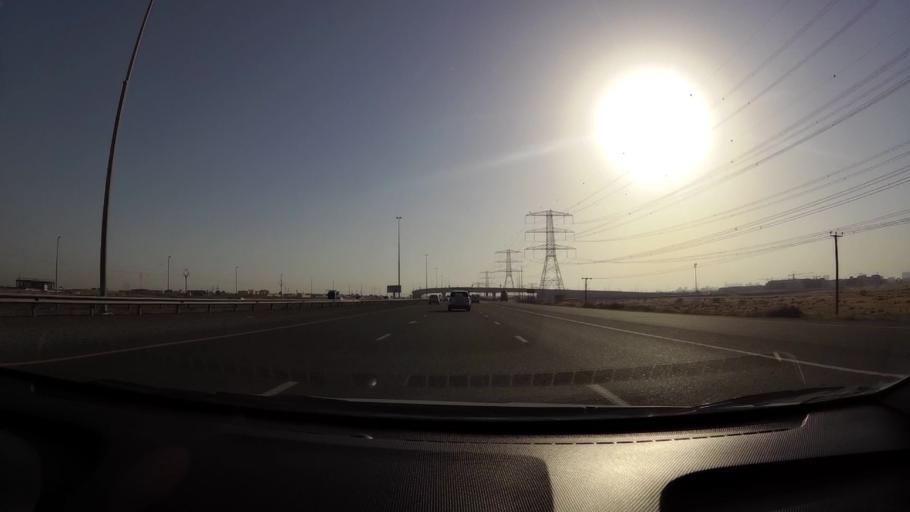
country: AE
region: Ajman
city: Ajman
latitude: 25.3601
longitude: 55.5186
